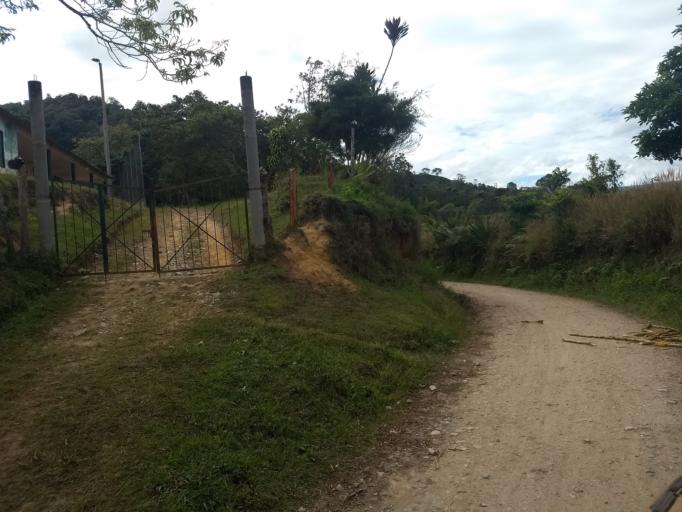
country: CO
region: Huila
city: San Agustin
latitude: 1.9102
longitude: -76.3182
